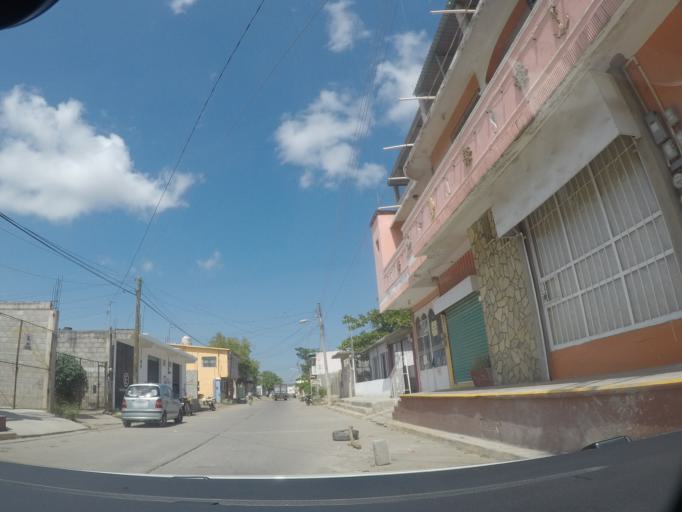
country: MX
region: Oaxaca
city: Juchitan de Zaragoza
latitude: 16.4350
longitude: -95.0171
